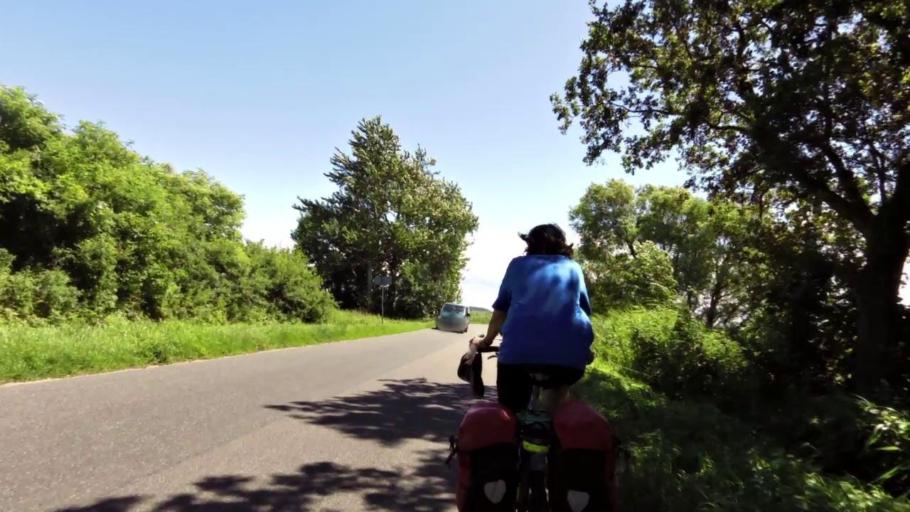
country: PL
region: West Pomeranian Voivodeship
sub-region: Koszalin
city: Koszalin
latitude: 54.2997
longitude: 16.2045
